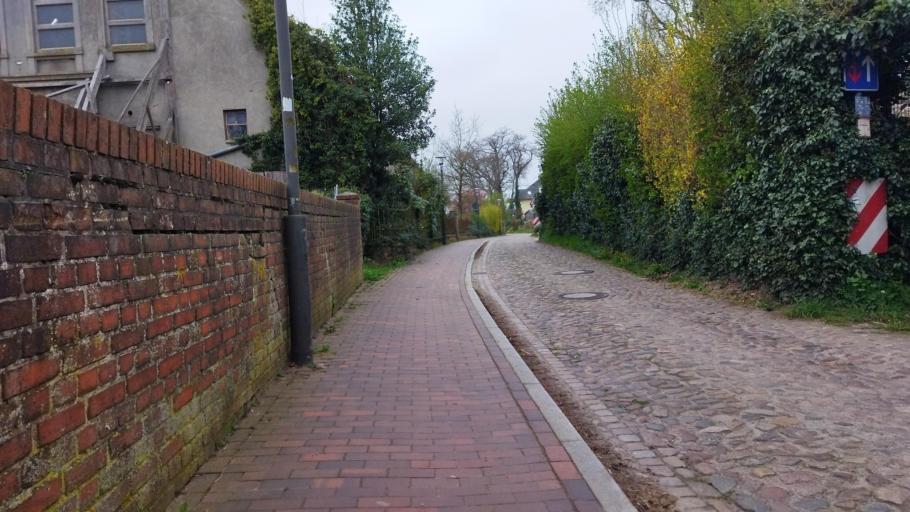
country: DE
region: Lower Saxony
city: Achim
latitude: 53.0108
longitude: 9.0297
